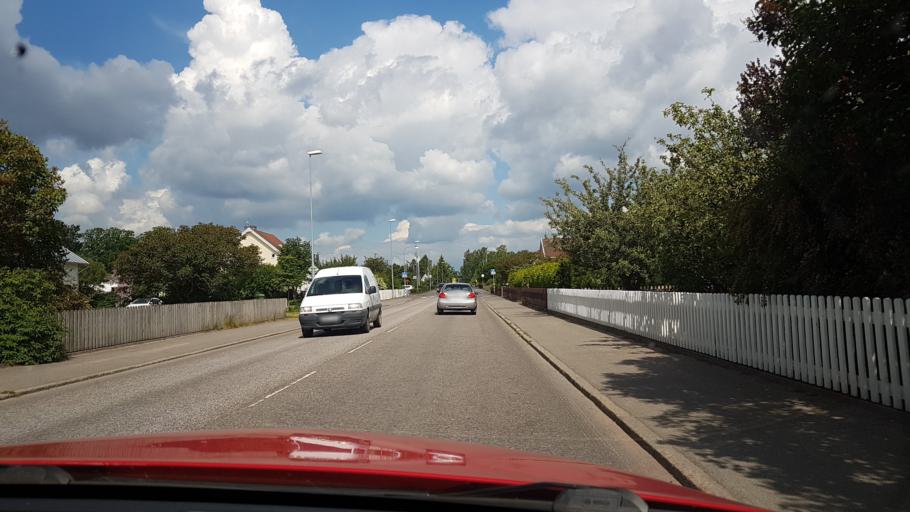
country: SE
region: Vaestra Goetaland
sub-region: Hjo Kommun
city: Hjo
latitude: 58.3084
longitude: 14.2846
